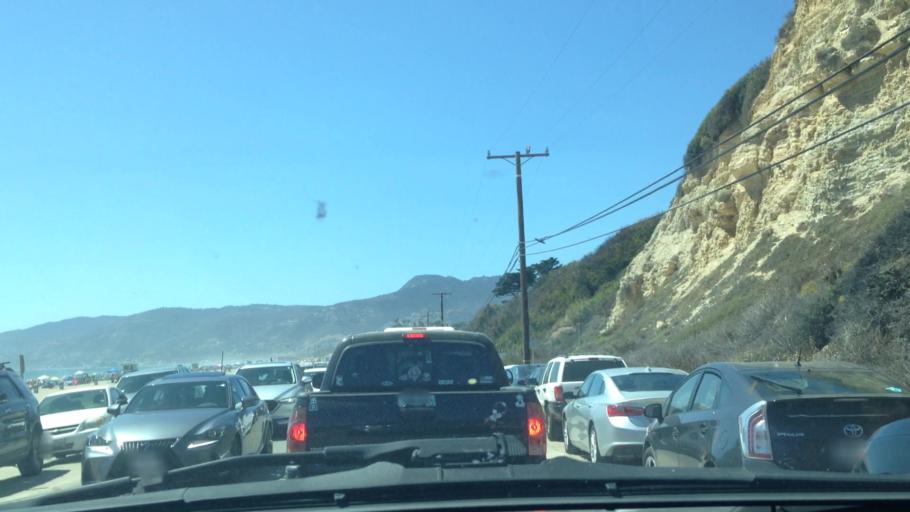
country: US
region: California
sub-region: Los Angeles County
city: Malibu
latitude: 34.0120
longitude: -118.8178
